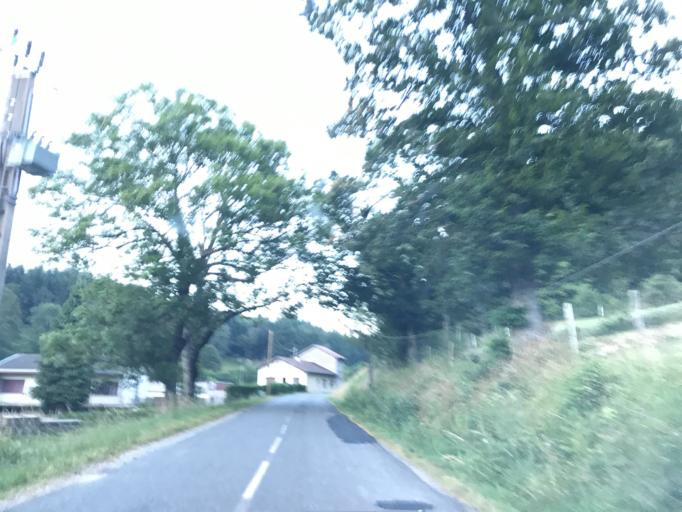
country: FR
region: Rhone-Alpes
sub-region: Departement de la Loire
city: Noiretable
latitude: 45.8209
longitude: 3.7098
